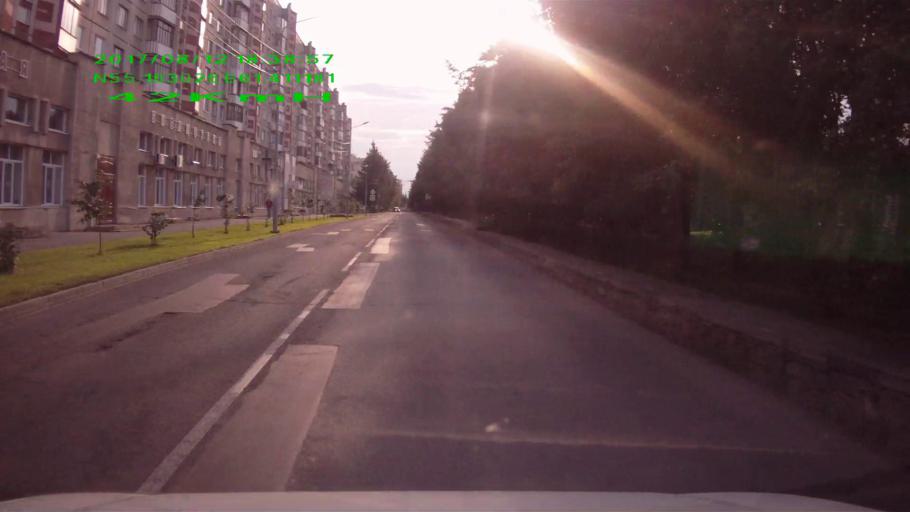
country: RU
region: Chelyabinsk
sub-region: Gorod Chelyabinsk
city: Chelyabinsk
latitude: 55.1621
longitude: 61.4065
